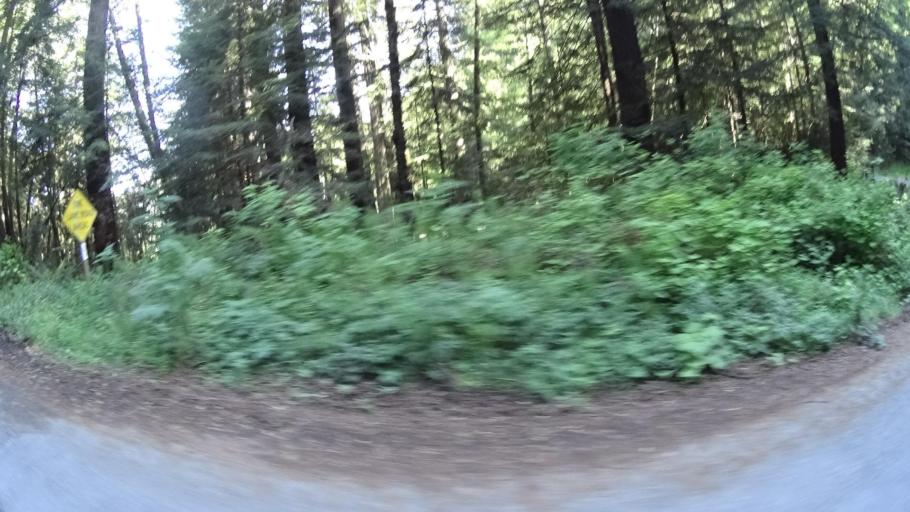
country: US
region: California
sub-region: Humboldt County
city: Rio Dell
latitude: 40.4501
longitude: -123.9795
